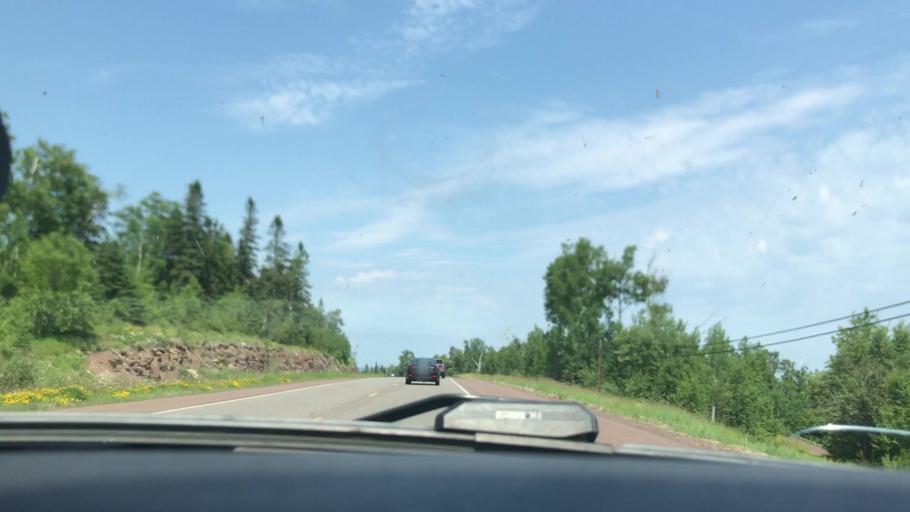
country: US
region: Minnesota
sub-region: Cook County
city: Grand Marais
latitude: 47.5930
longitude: -90.7992
